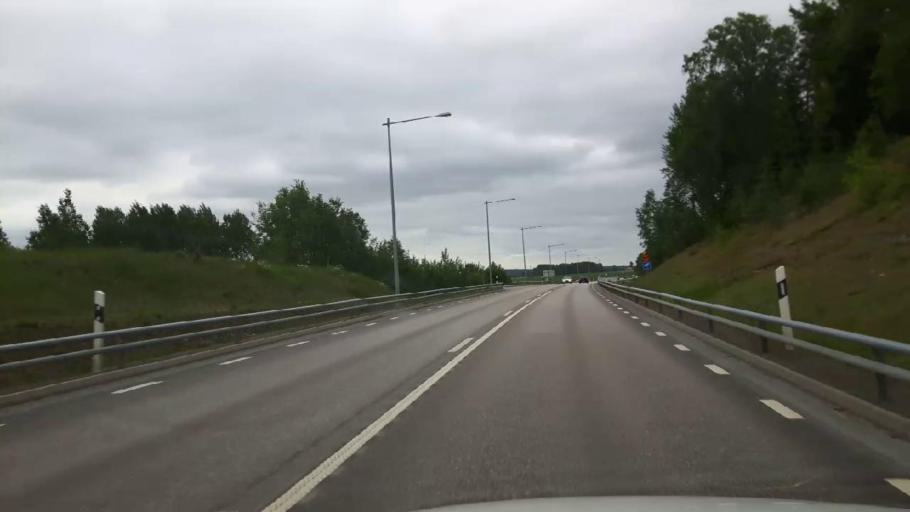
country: SE
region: Vaestmanland
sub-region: Kopings Kommun
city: Koping
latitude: 59.5506
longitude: 15.9125
